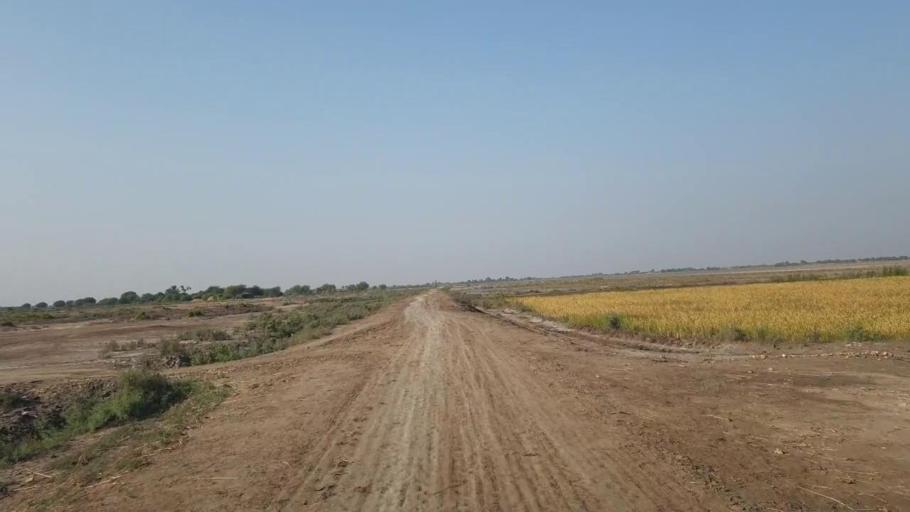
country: PK
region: Sindh
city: Kario
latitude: 24.9070
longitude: 68.6194
